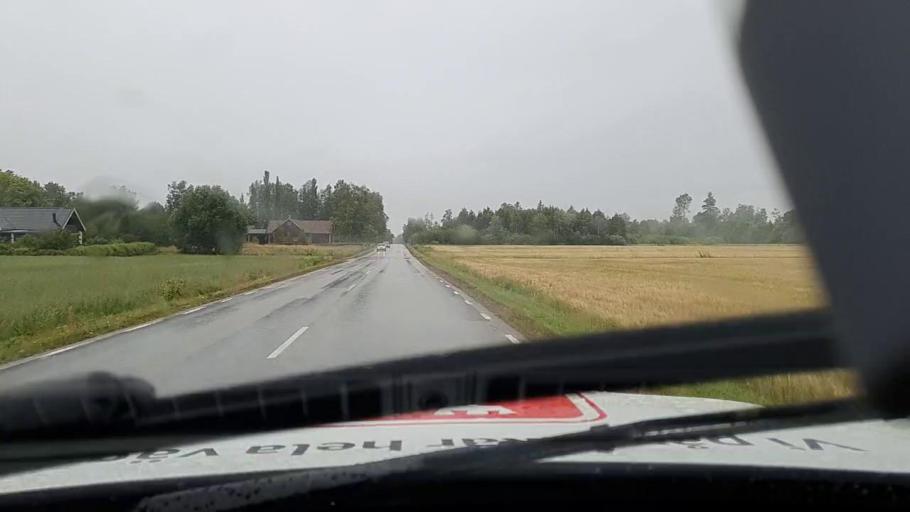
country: SE
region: Vaestra Goetaland
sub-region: Toreboda Kommun
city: Toereboda
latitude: 58.6989
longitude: 14.1344
